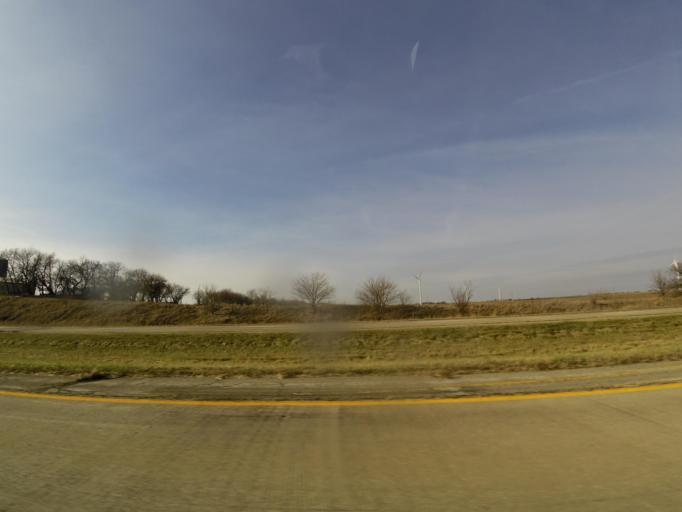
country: US
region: Illinois
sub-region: Macon County
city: Maroa
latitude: 40.0415
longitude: -88.9653
